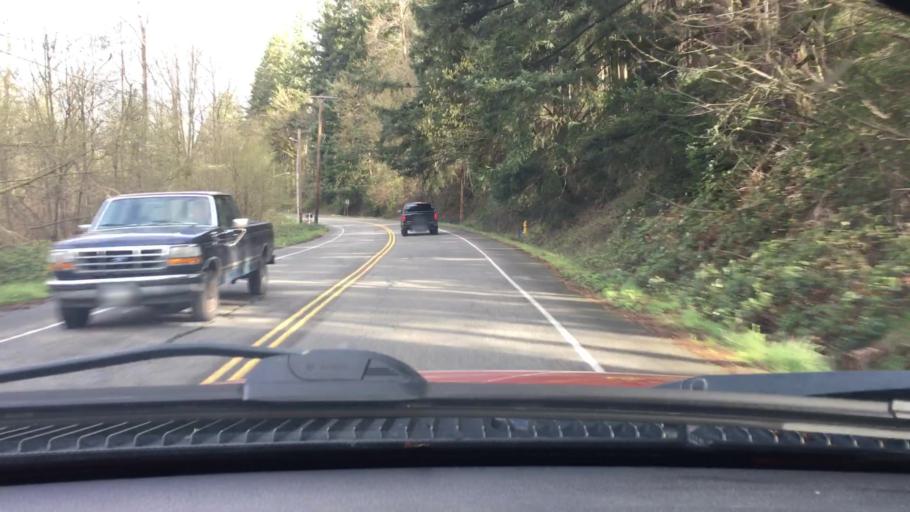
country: US
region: Washington
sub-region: King County
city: Maple Valley
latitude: 47.3686
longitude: -122.0439
